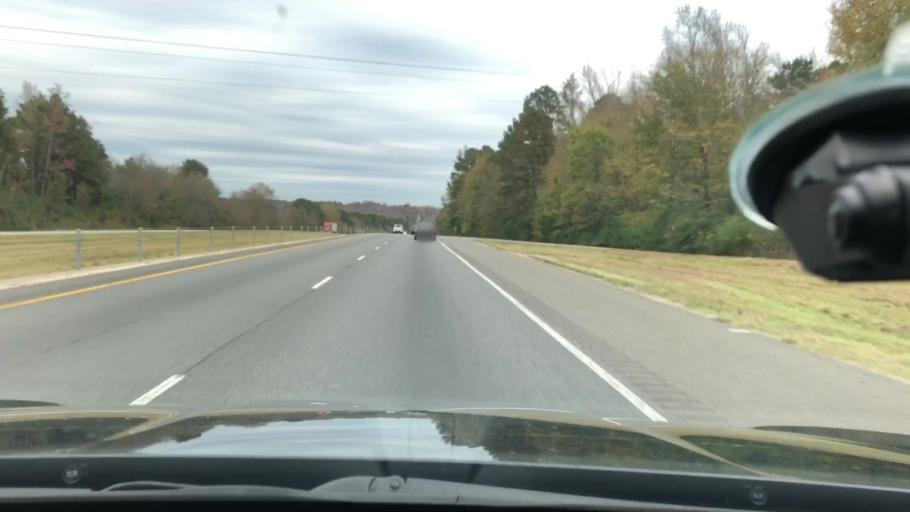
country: US
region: Arkansas
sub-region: Hot Spring County
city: Malvern
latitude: 34.3347
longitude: -92.9172
